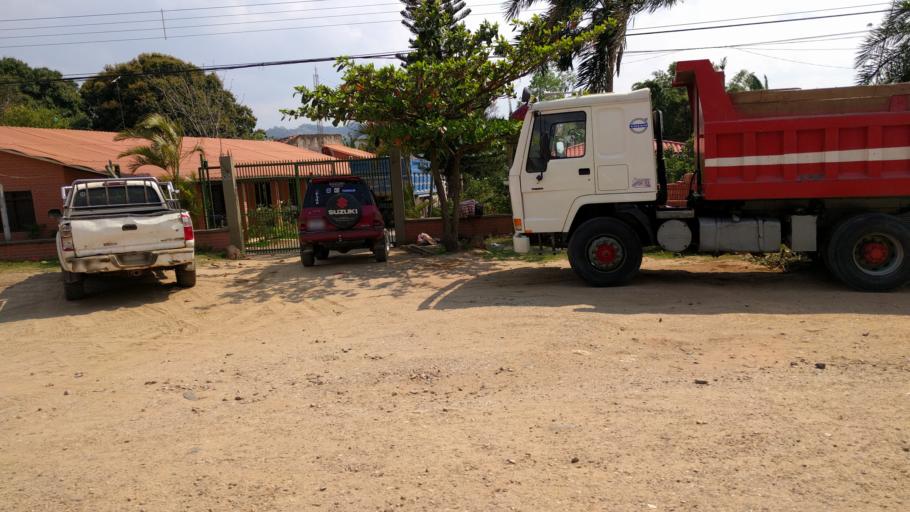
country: BO
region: Santa Cruz
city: Santa Rita
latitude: -17.9658
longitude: -63.3626
